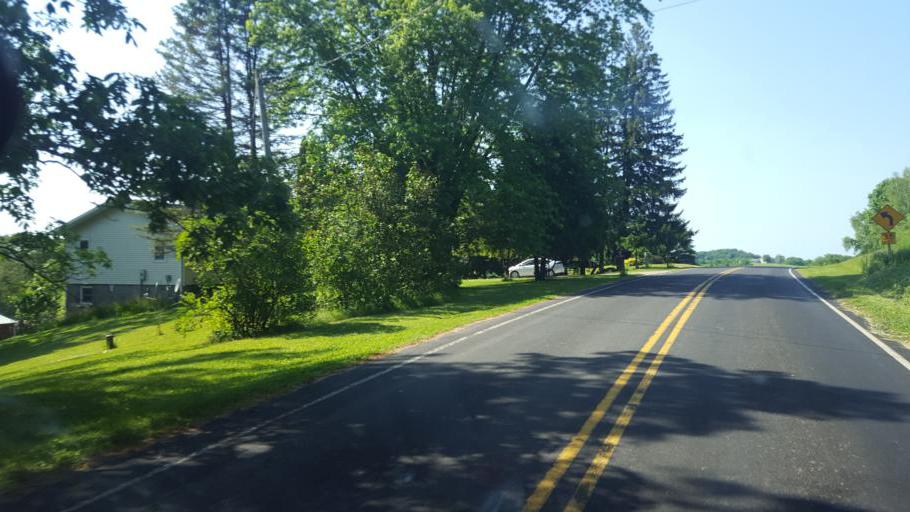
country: US
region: Wisconsin
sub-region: Vernon County
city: Hillsboro
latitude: 43.6622
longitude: -90.3463
